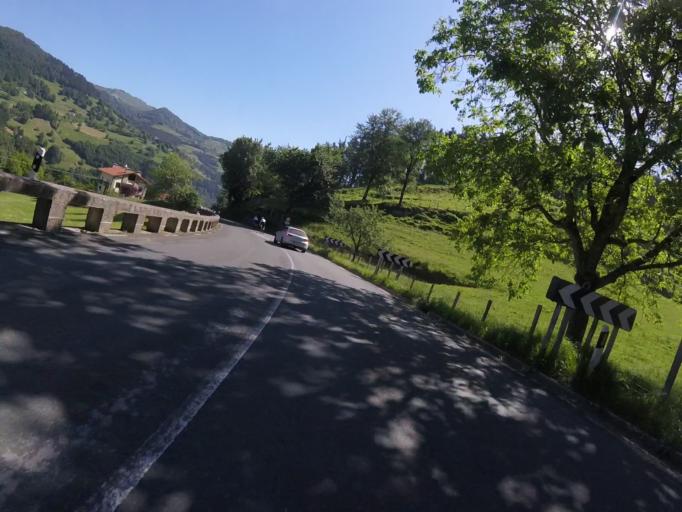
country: ES
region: Basque Country
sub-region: Provincia de Guipuzcoa
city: Albiztur
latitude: 43.1241
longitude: -2.1393
